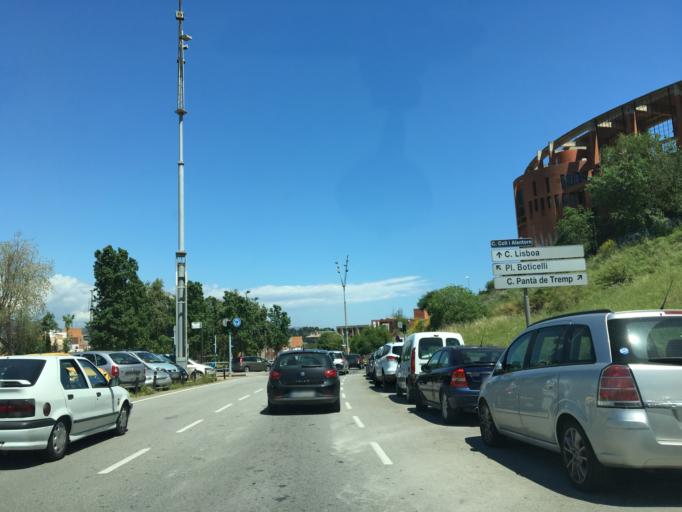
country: ES
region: Catalonia
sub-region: Provincia de Barcelona
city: Horta-Guinardo
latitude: 41.4255
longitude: 2.1494
